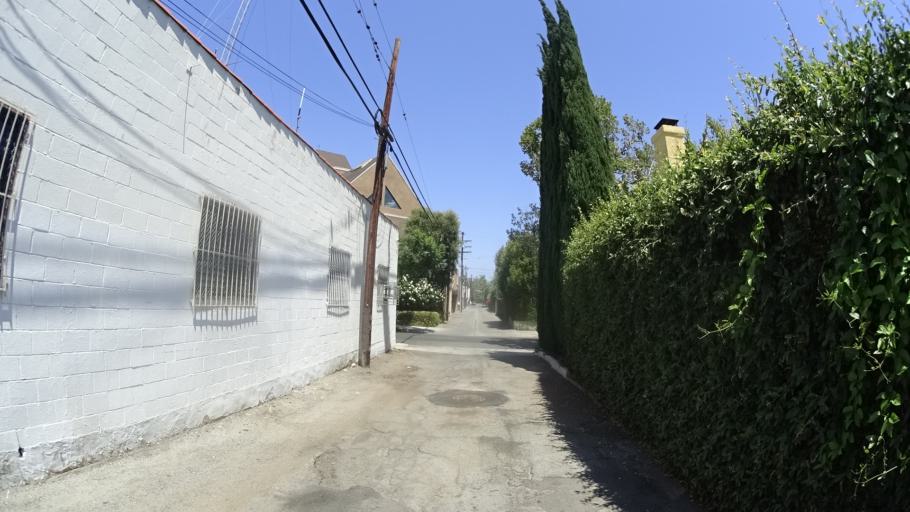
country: US
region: California
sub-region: Los Angeles County
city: Hollywood
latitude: 34.0830
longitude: -118.3409
